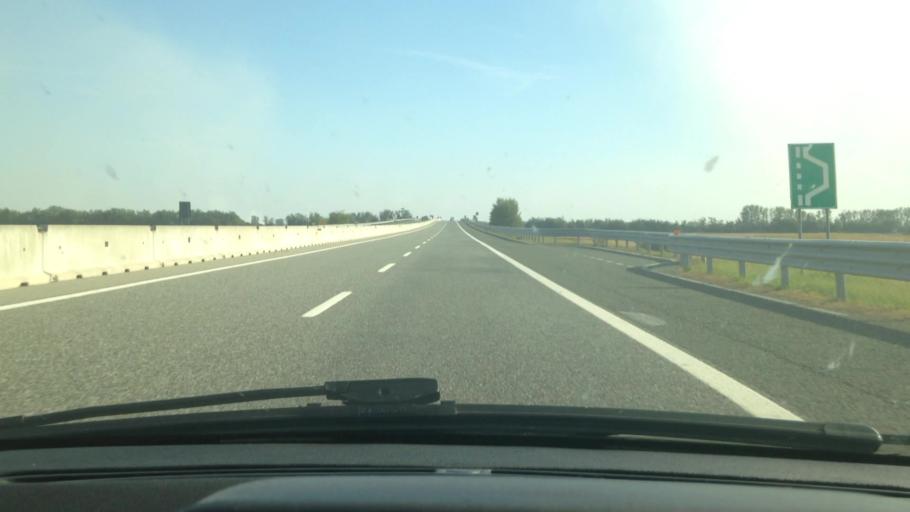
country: IT
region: Piedmont
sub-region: Provincia di Vercelli
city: Crova
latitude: 45.3415
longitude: 8.2097
